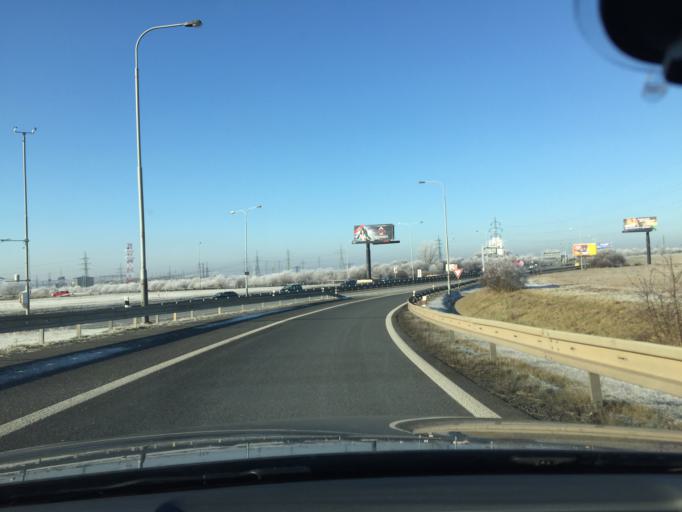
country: CZ
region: Central Bohemia
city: Cernosice
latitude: 50.0158
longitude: 14.3402
